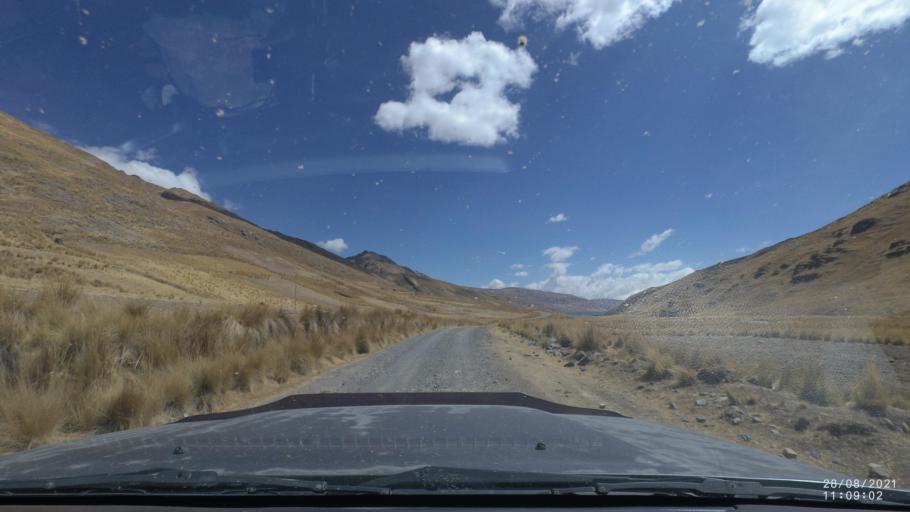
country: BO
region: Cochabamba
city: Cochabamba
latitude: -17.1638
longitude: -66.3060
